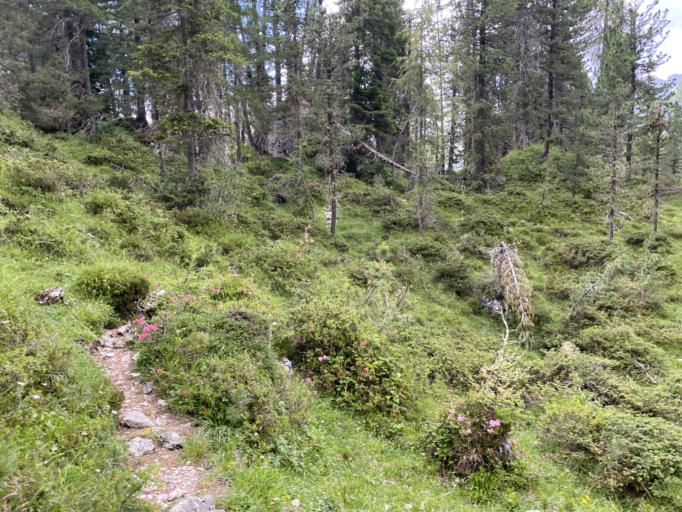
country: IT
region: Trentino-Alto Adige
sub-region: Bolzano
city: Selva
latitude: 46.6226
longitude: 11.7738
